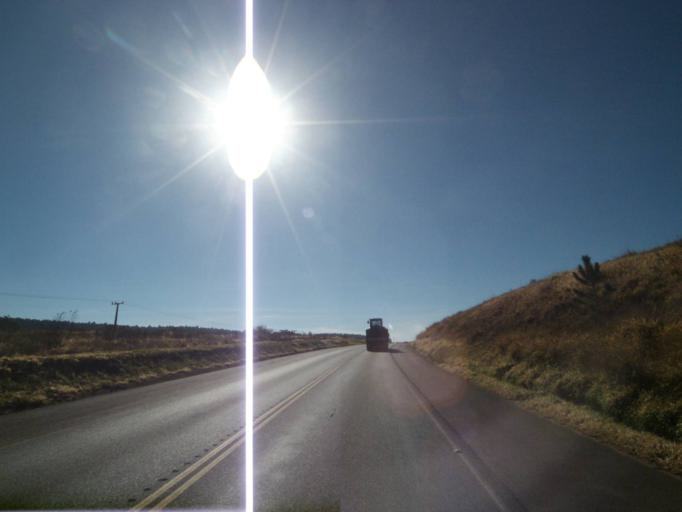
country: BR
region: Parana
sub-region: Tibagi
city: Tibagi
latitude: -24.4656
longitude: -50.4387
